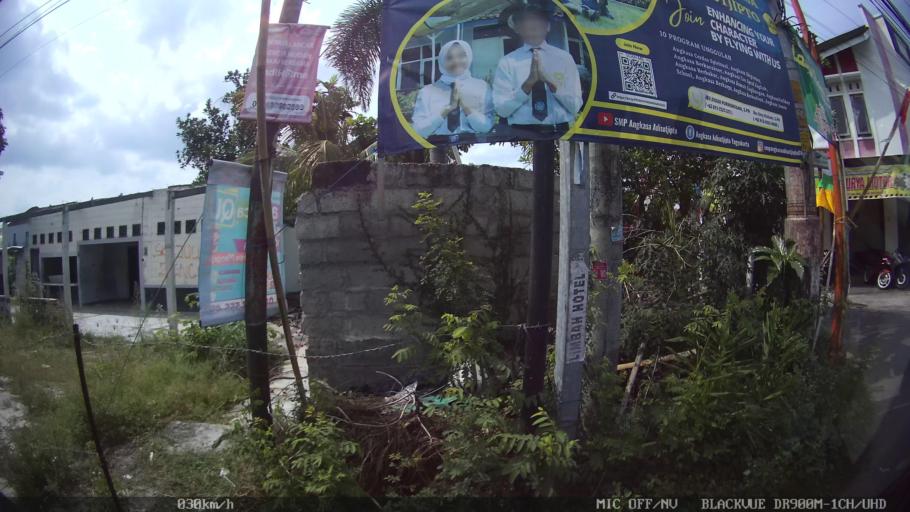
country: ID
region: Daerah Istimewa Yogyakarta
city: Yogyakarta
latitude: -7.7925
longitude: 110.4014
